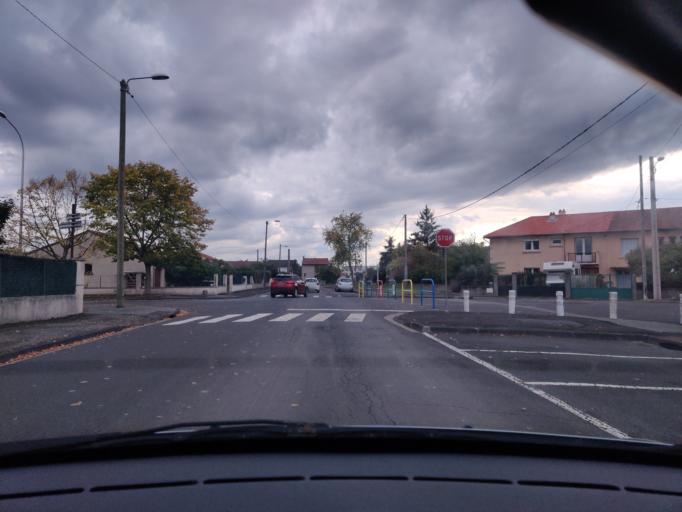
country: FR
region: Auvergne
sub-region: Departement du Puy-de-Dome
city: Menetrol
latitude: 45.8828
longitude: 3.1273
